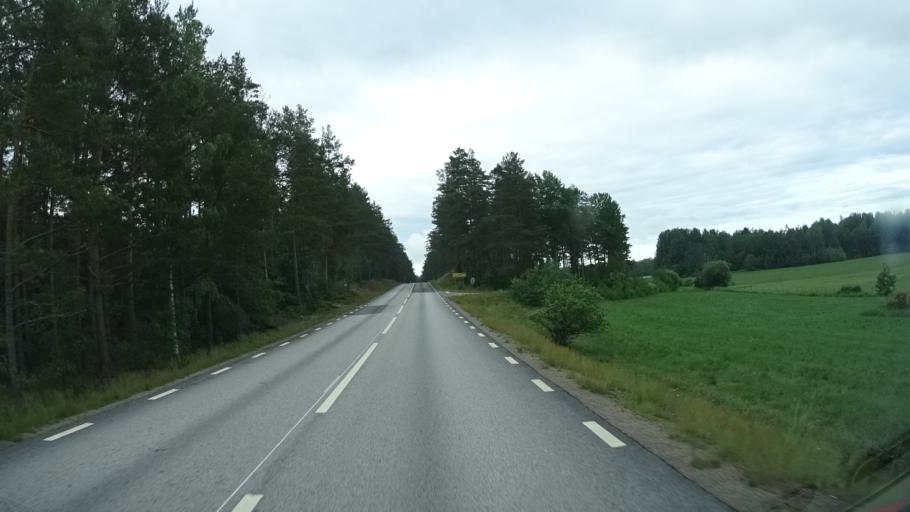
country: SE
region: Kalmar
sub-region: Oskarshamns Kommun
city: Oskarshamn
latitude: 57.3114
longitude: 16.2811
